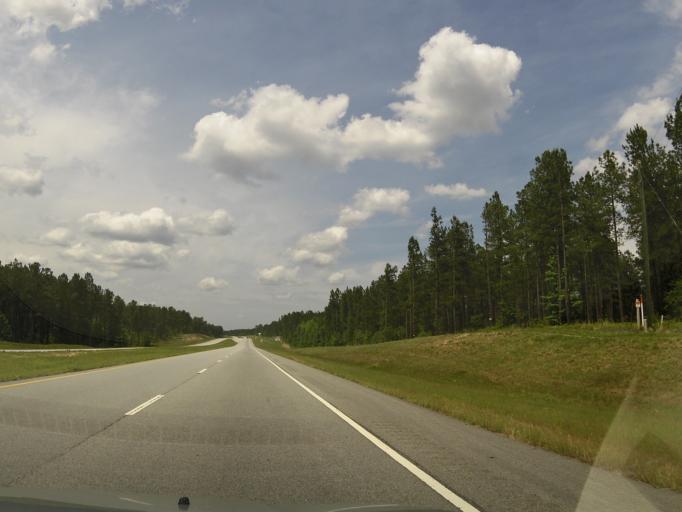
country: US
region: Georgia
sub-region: Emanuel County
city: Swainsboro
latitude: 32.7018
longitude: -82.3908
